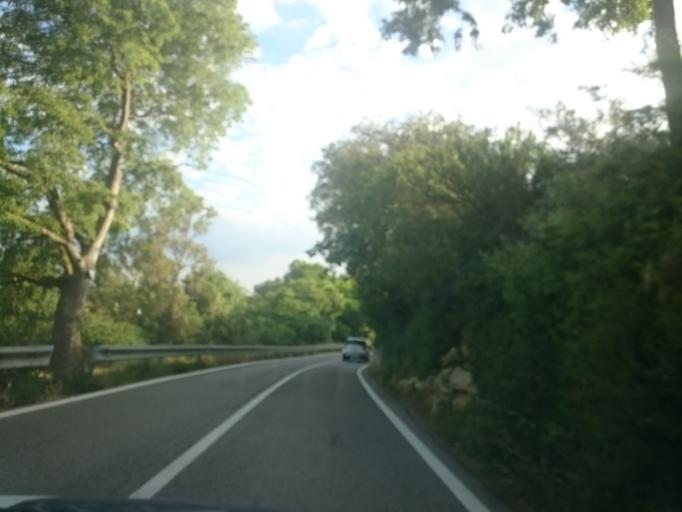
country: ES
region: Catalonia
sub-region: Provincia de Barcelona
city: Castellet
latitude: 41.2622
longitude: 1.6331
